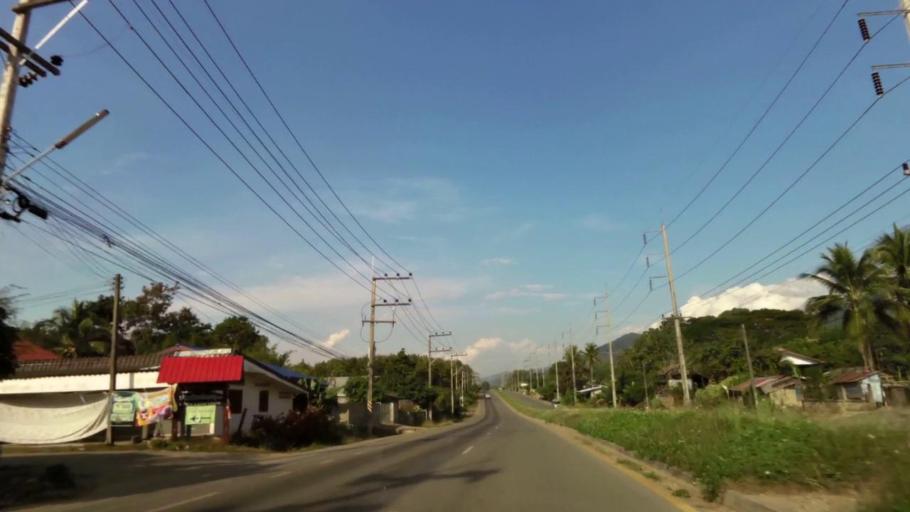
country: TH
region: Chiang Rai
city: Khun Tan
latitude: 19.8724
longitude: 100.2865
